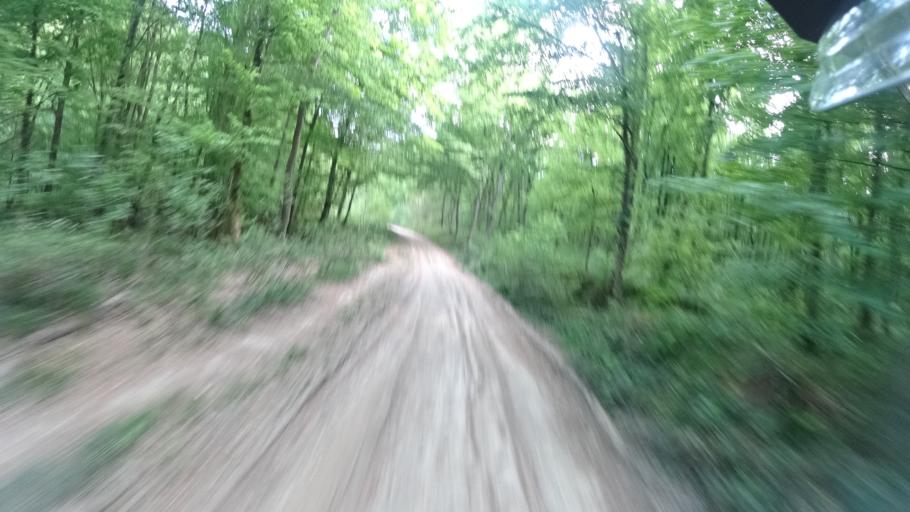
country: HR
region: Zagrebacka
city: Jablanovec
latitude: 45.8660
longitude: 15.8968
